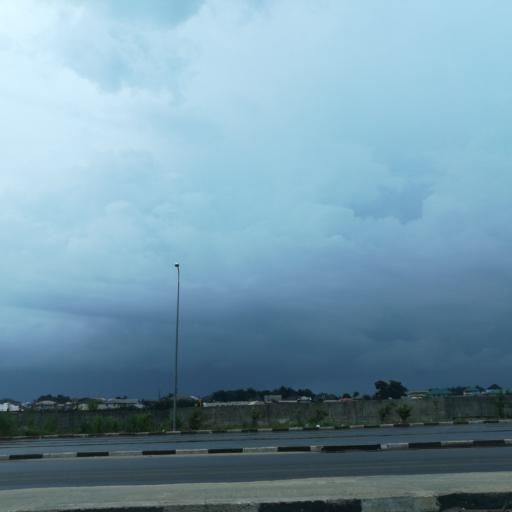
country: NG
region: Rivers
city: Port Harcourt
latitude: 4.8016
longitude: 7.0554
